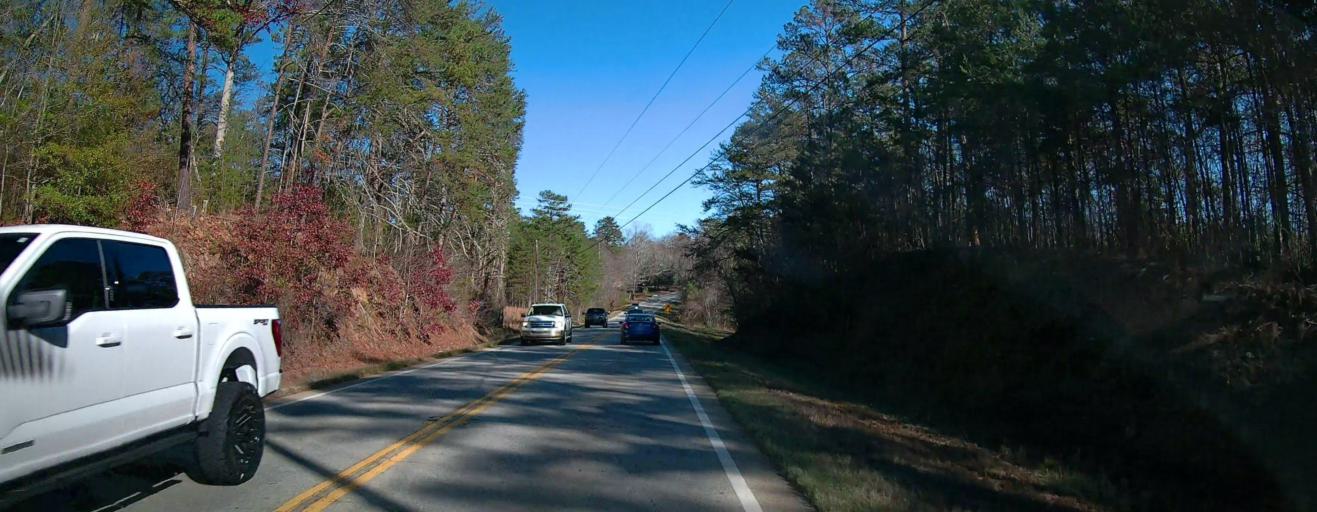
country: US
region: Georgia
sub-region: Hall County
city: Lula
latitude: 34.4058
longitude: -83.7043
